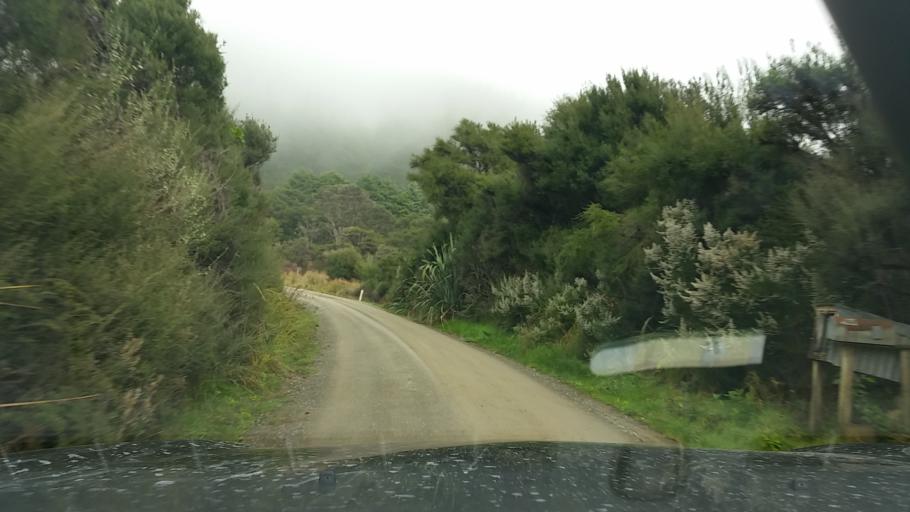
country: NZ
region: Marlborough
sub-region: Marlborough District
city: Picton
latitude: -41.1699
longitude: 174.0021
